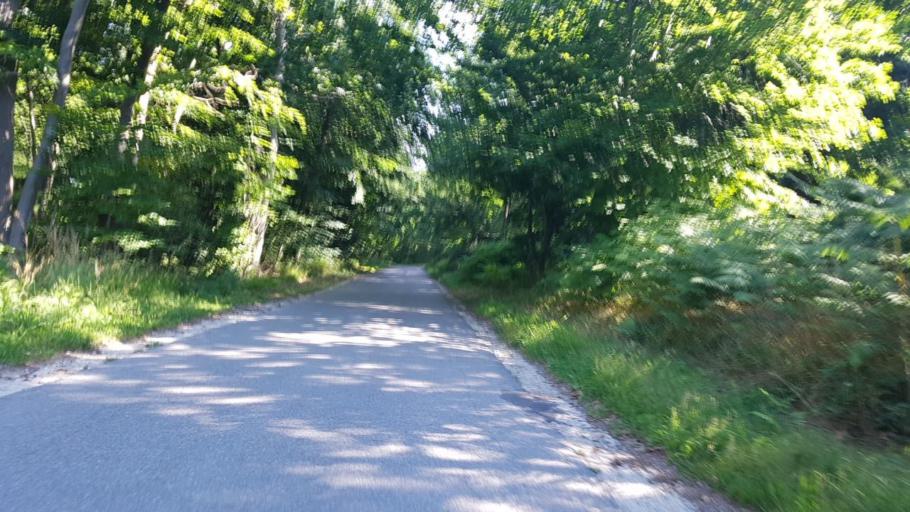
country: FR
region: Picardie
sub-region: Departement de l'Oise
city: Pont-Sainte-Maxence
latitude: 49.2786
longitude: 2.6225
